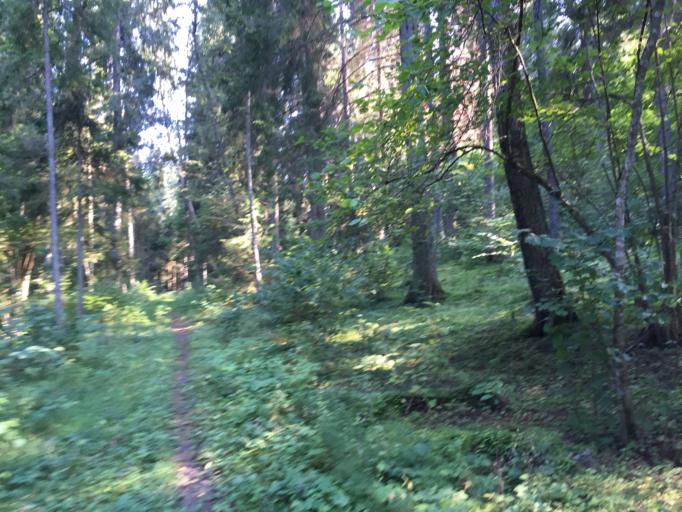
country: LV
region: Limbazu Rajons
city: Limbazi
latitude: 57.5667
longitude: 24.7998
